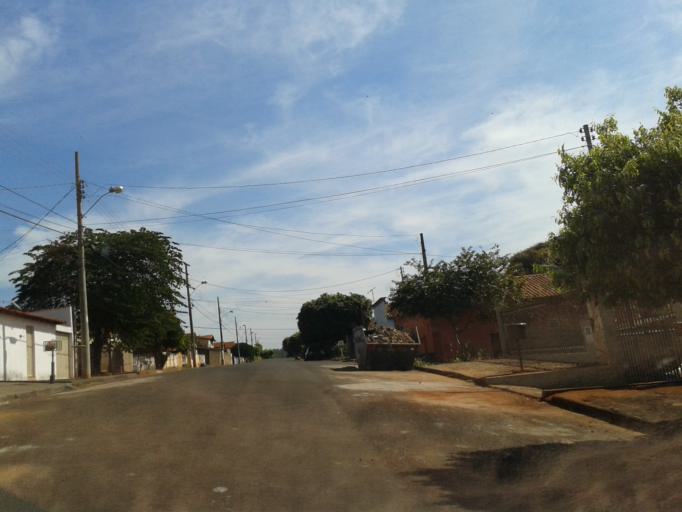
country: BR
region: Minas Gerais
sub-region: Ituiutaba
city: Ituiutaba
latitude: -18.9630
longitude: -49.4643
